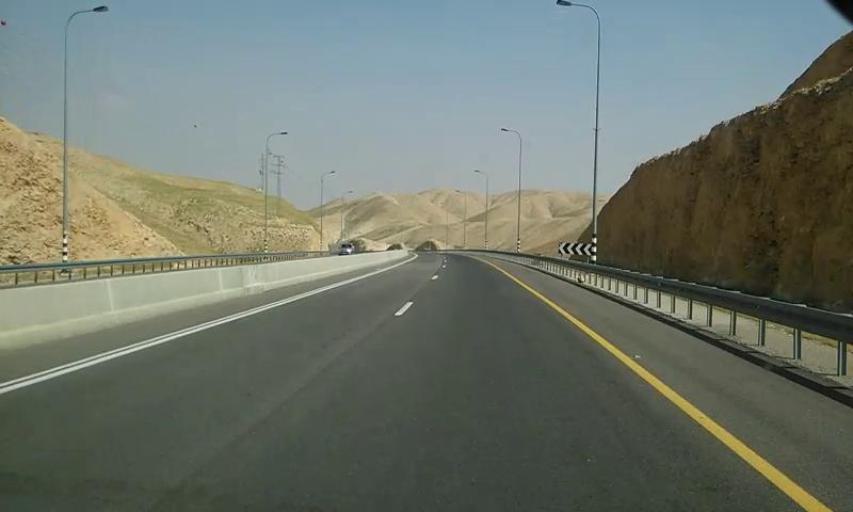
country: PS
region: West Bank
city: Jericho
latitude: 31.8157
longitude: 35.3675
